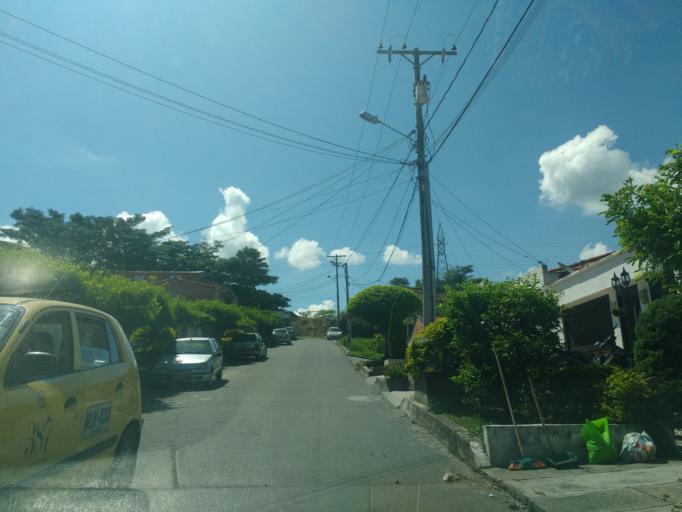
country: CO
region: Valle del Cauca
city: Cartago
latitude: 4.7527
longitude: -75.8986
